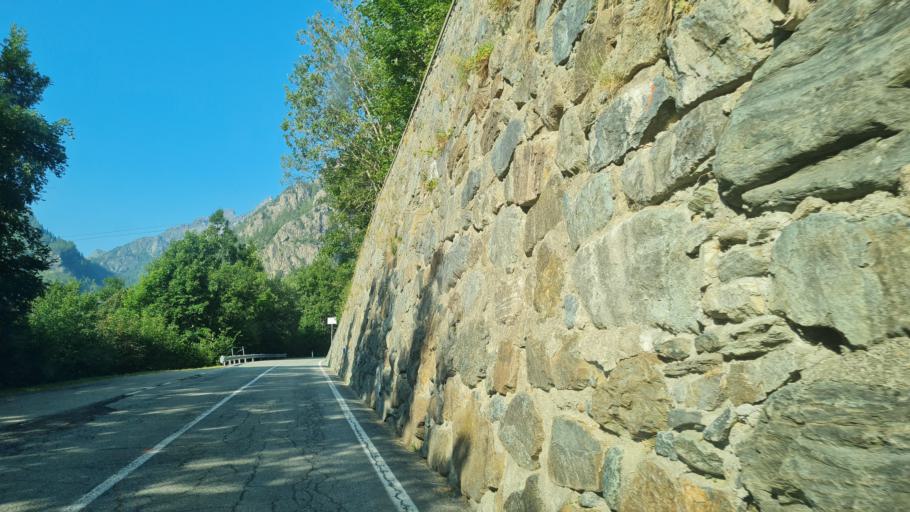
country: IT
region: Aosta Valley
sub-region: Valle d'Aosta
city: Champorcher
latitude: 45.6215
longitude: 7.6434
